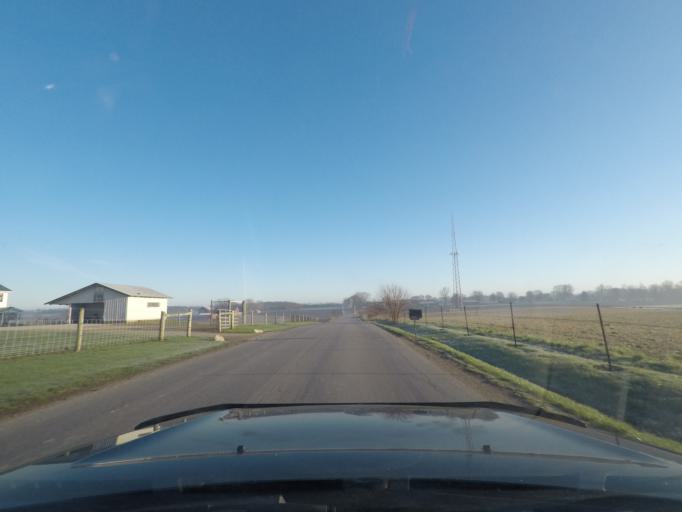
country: US
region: Indiana
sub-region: Elkhart County
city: Dunlap
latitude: 41.5468
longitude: -85.9247
